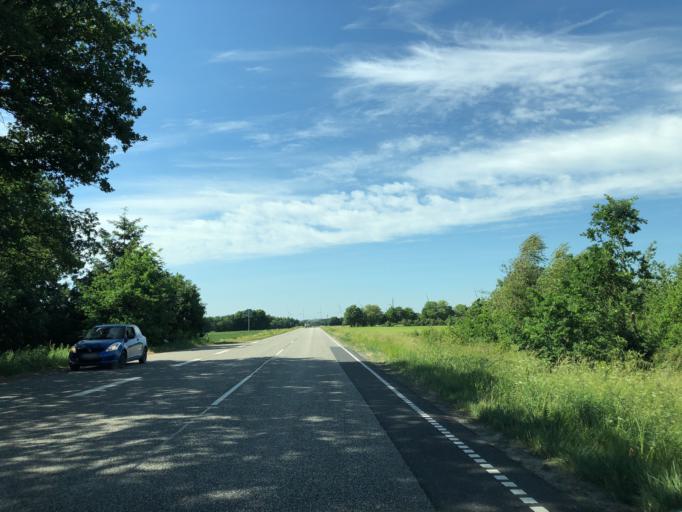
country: DK
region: South Denmark
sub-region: Vejle Kommune
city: Give
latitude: 55.8939
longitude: 9.2100
